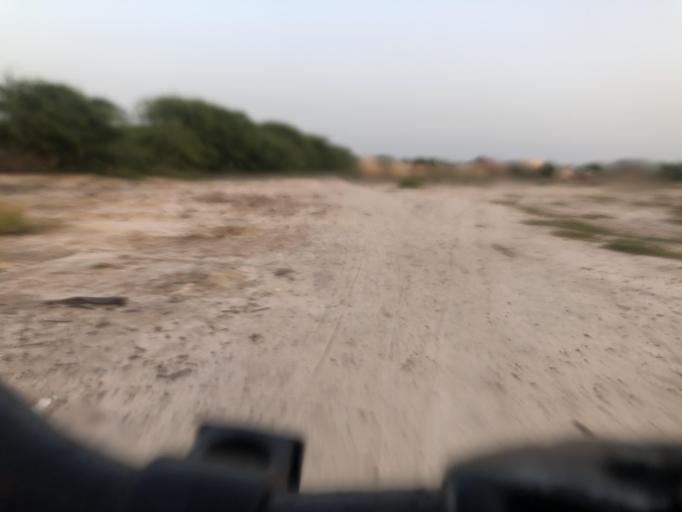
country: SN
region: Saint-Louis
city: Saint-Louis
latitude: 16.0728
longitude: -16.4317
